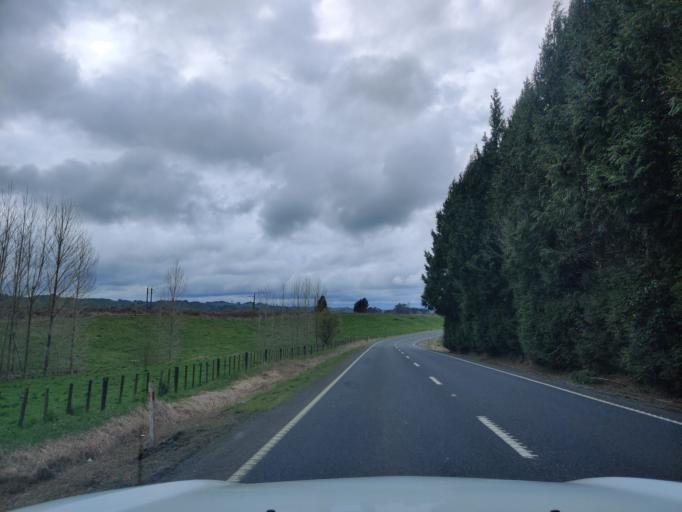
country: NZ
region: Waikato
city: Turangi
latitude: -39.0335
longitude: 175.3821
